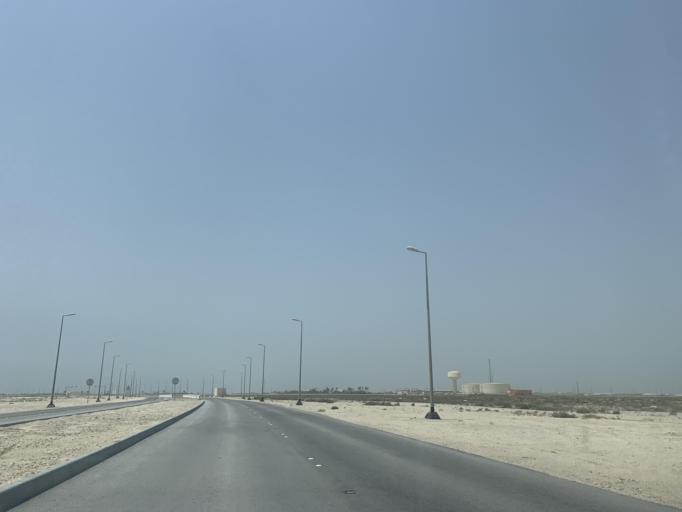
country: BH
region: Central Governorate
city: Dar Kulayb
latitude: 25.8437
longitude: 50.5936
